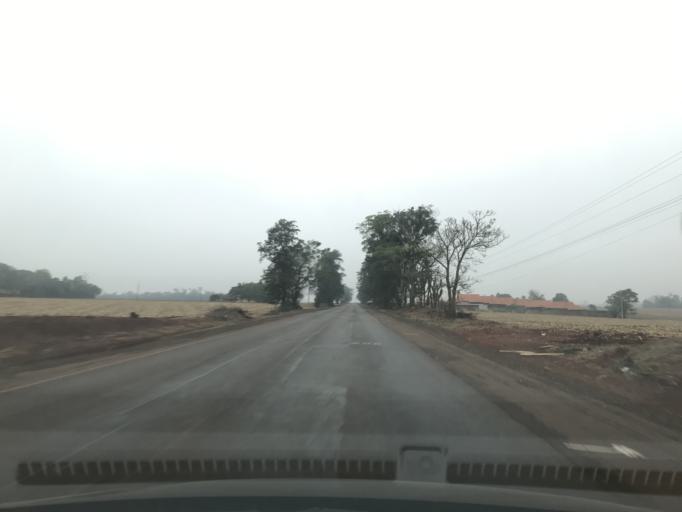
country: BR
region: Parana
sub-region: Palotina
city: Palotina
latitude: -24.3729
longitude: -53.8352
